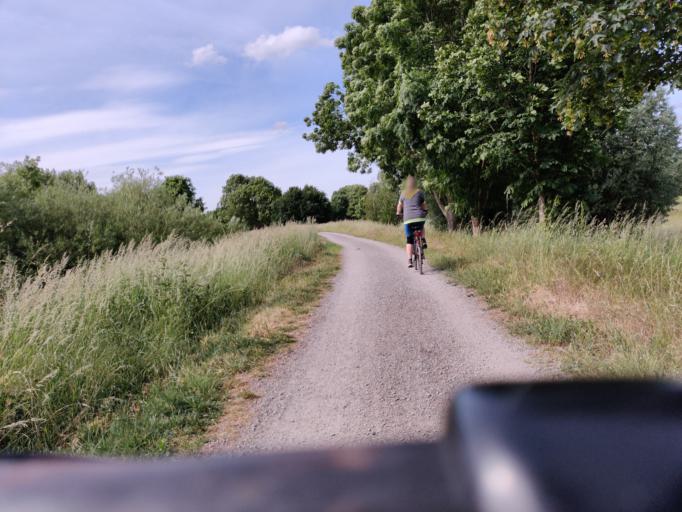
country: DE
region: Lower Saxony
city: Wunstorf
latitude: 52.4328
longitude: 9.4381
